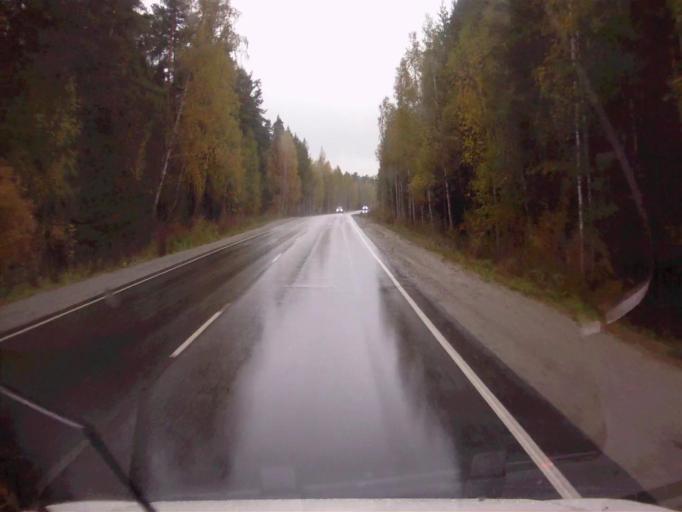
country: RU
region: Chelyabinsk
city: Kyshtym
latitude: 55.6524
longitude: 60.5775
